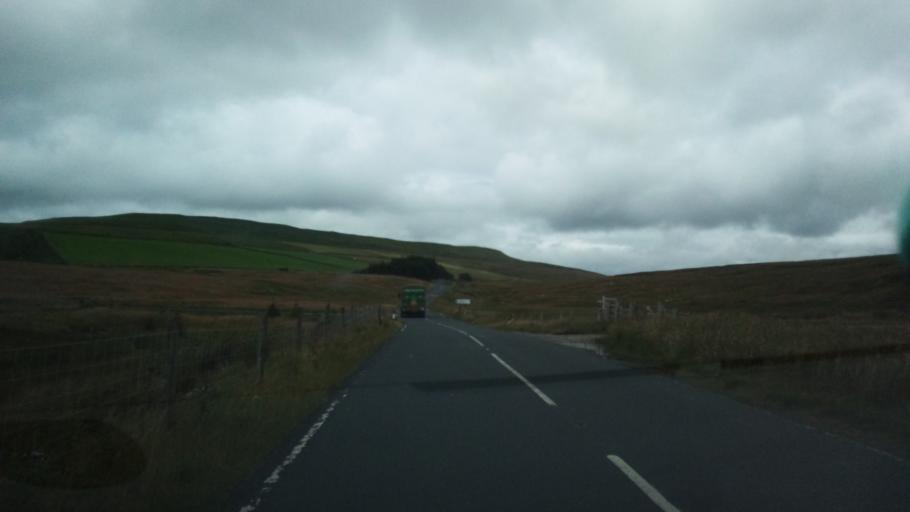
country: GB
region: England
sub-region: North Yorkshire
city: Ingleton
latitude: 54.2468
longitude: -2.3160
